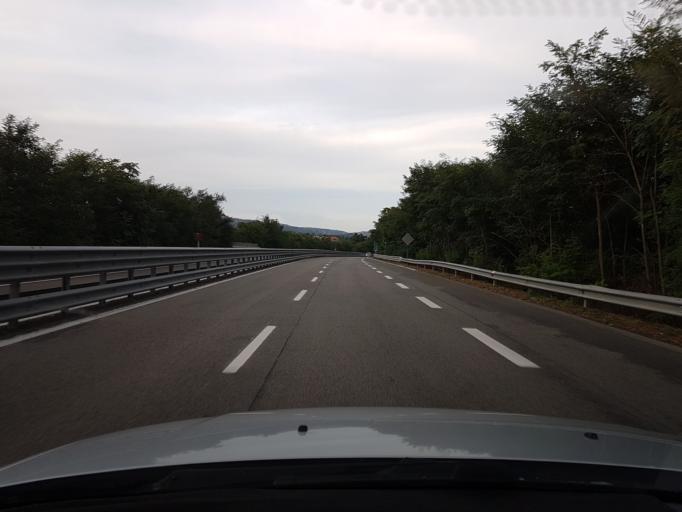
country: IT
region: Sardinia
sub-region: Provincia di Nuoro
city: Nuoro
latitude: 40.3243
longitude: 9.2812
